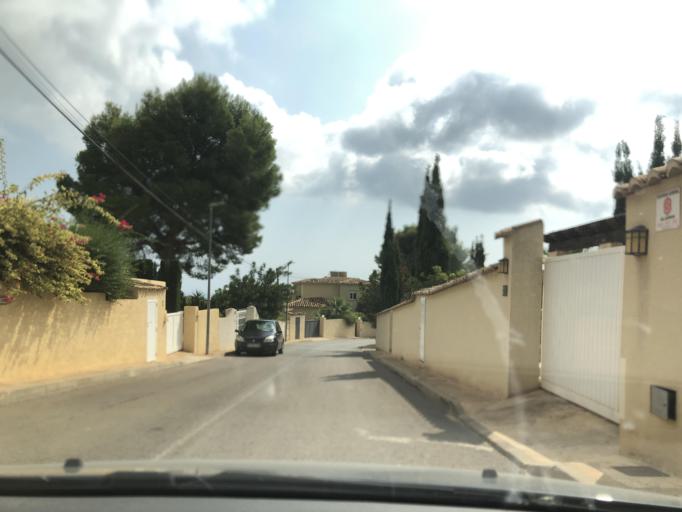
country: ES
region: Valencia
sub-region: Provincia de Alicante
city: Altea
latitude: 38.6379
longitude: -0.0665
